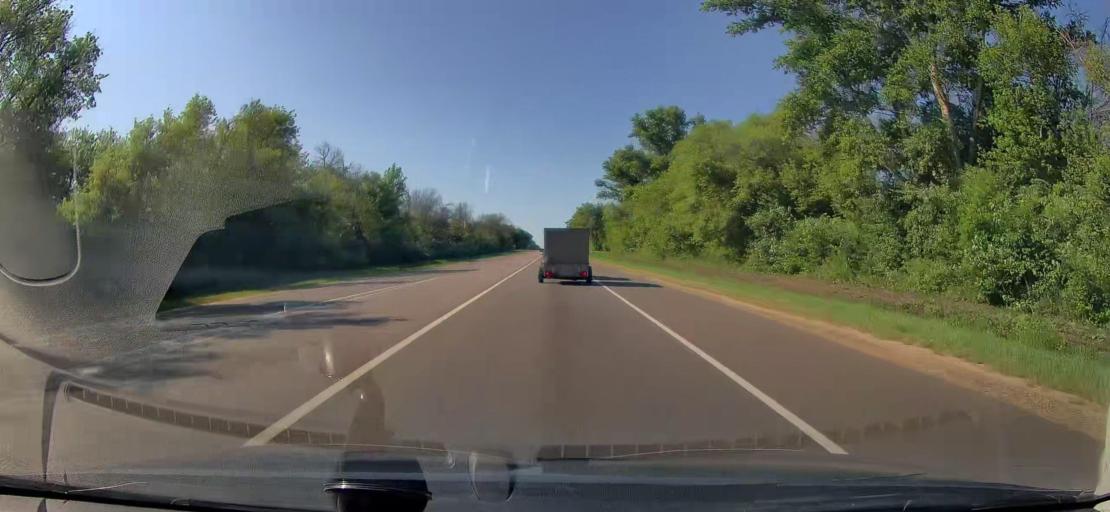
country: RU
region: Orjol
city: Kromy
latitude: 52.6073
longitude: 35.7620
